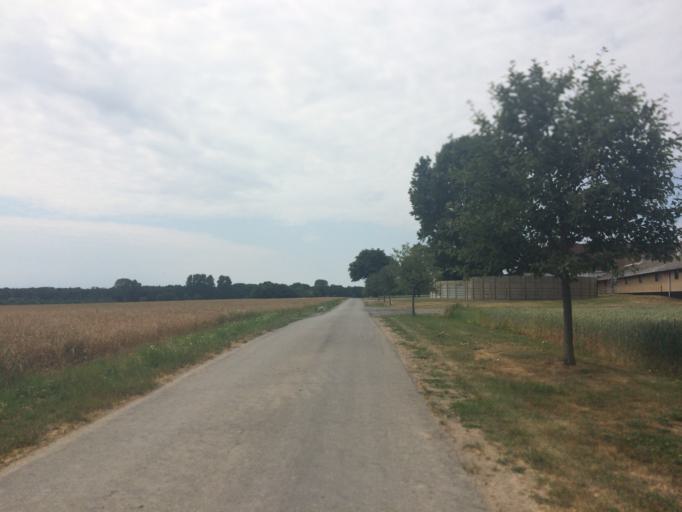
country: DK
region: Capital Region
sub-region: Bornholm Kommune
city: Ronne
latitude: 55.1762
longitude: 14.7298
